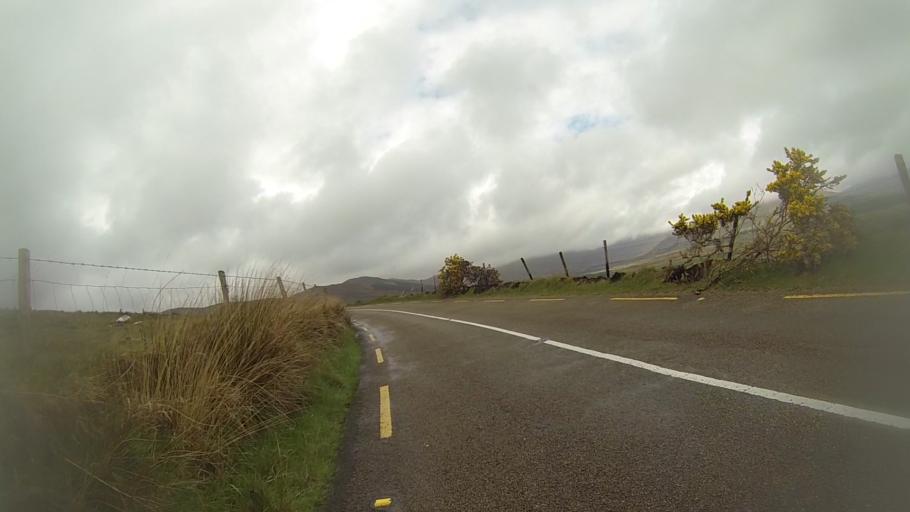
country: IE
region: Munster
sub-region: Ciarrai
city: Kenmare
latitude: 51.8813
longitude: -9.7929
